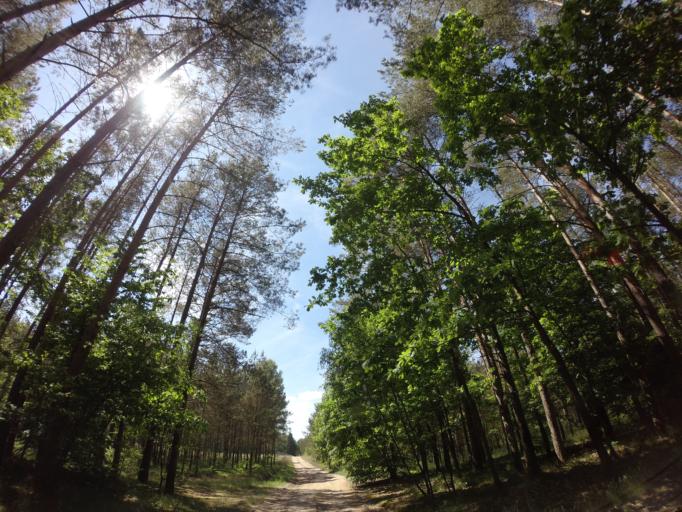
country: PL
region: West Pomeranian Voivodeship
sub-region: Powiat choszczenski
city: Drawno
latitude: 53.1631
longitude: 15.8816
